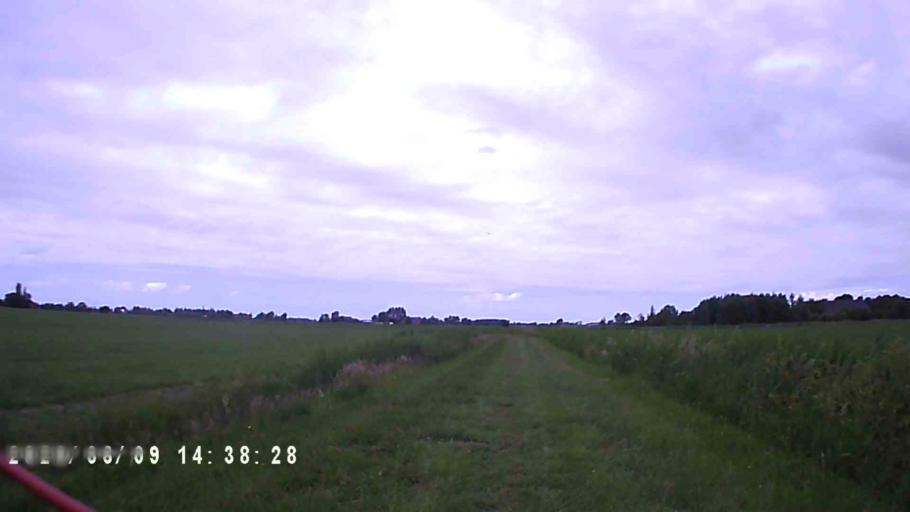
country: NL
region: Groningen
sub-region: Gemeente Bedum
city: Bedum
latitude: 53.3292
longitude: 6.5774
